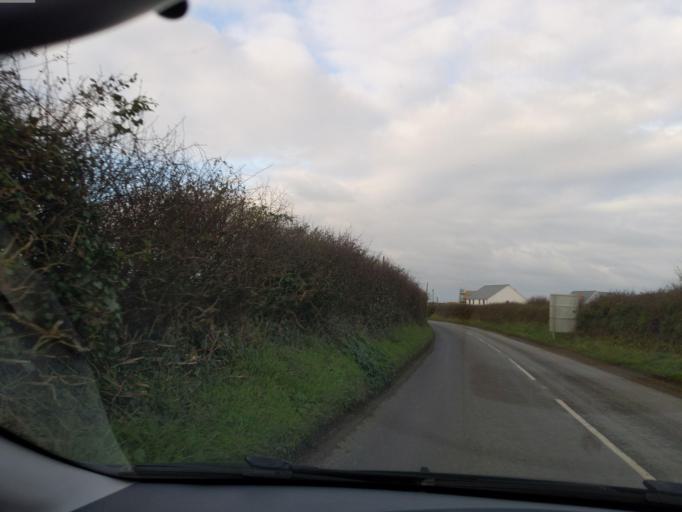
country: GB
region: England
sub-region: Cornwall
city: Padstow
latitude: 50.5340
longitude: -4.9515
